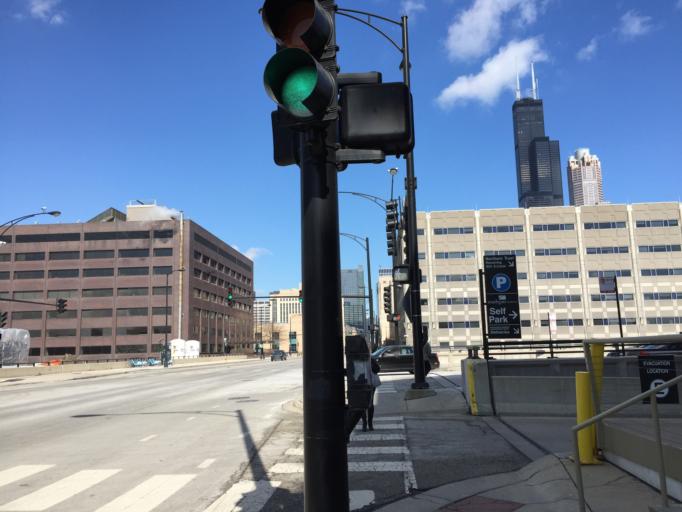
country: US
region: Illinois
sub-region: Cook County
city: Chicago
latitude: 41.8695
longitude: -87.6392
